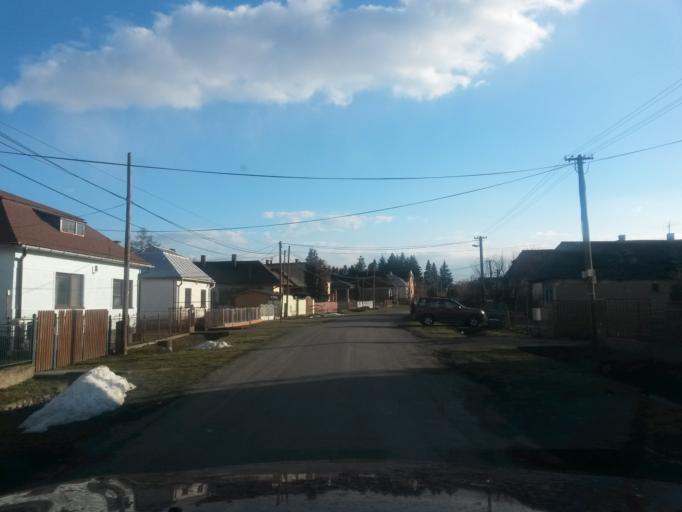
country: SK
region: Kosicky
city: Sobrance
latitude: 48.7743
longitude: 22.0848
